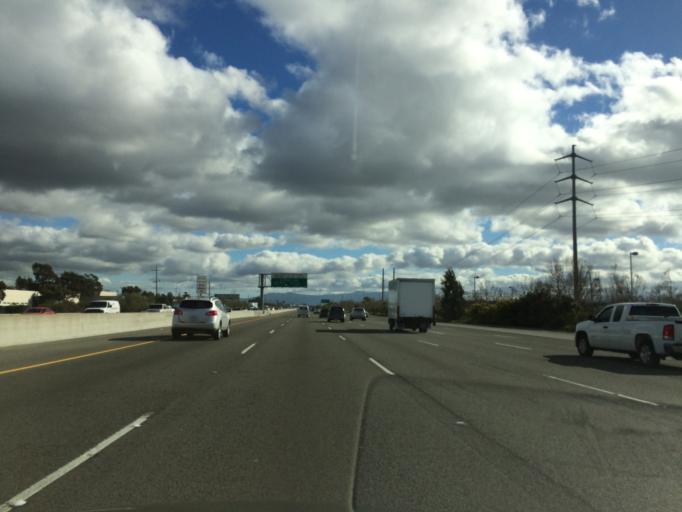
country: US
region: California
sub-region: Santa Clara County
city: Milpitas
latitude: 37.4514
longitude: -121.9225
